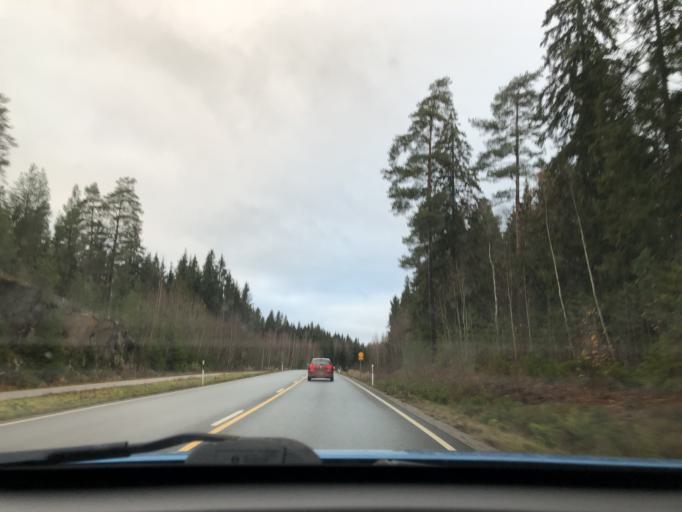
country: FI
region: Pirkanmaa
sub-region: Tampere
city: Kangasala
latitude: 61.4930
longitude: 24.0517
